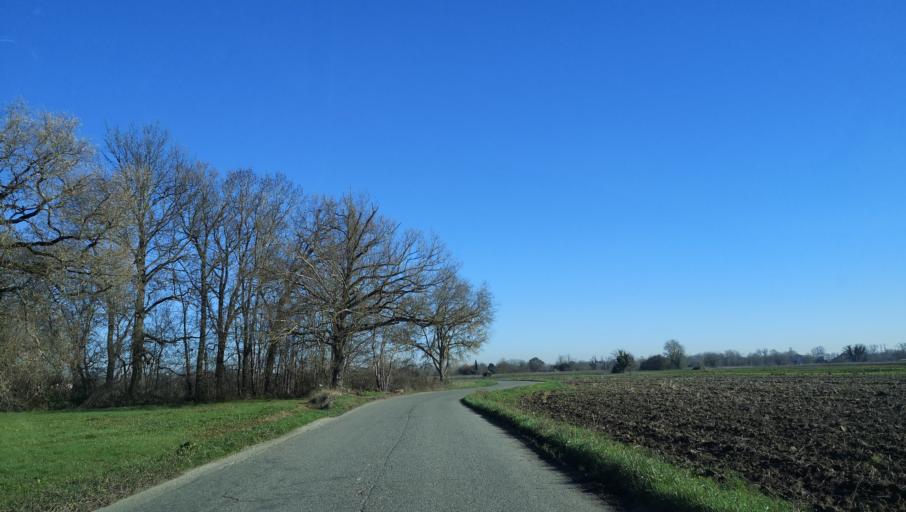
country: FR
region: Midi-Pyrenees
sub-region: Departement de la Haute-Garonne
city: Beauzelle
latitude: 43.6540
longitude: 1.3902
